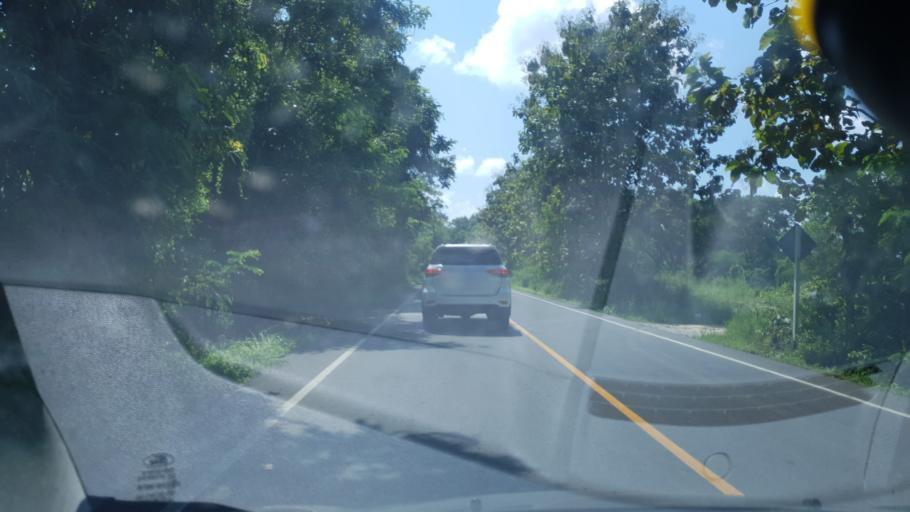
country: TH
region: Chiang Rai
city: Wiang Chai
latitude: 19.9386
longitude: 99.9178
